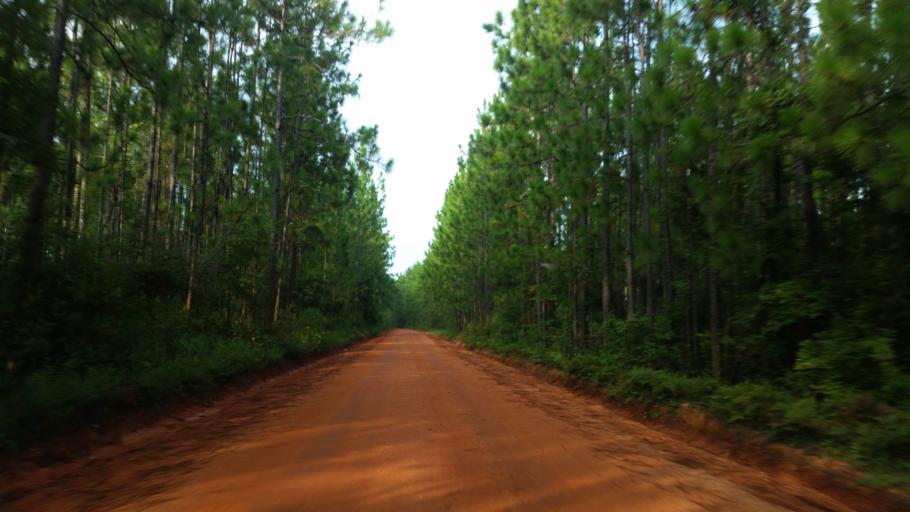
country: US
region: Alabama
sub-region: Escambia County
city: Atmore
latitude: 30.9292
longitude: -87.5707
